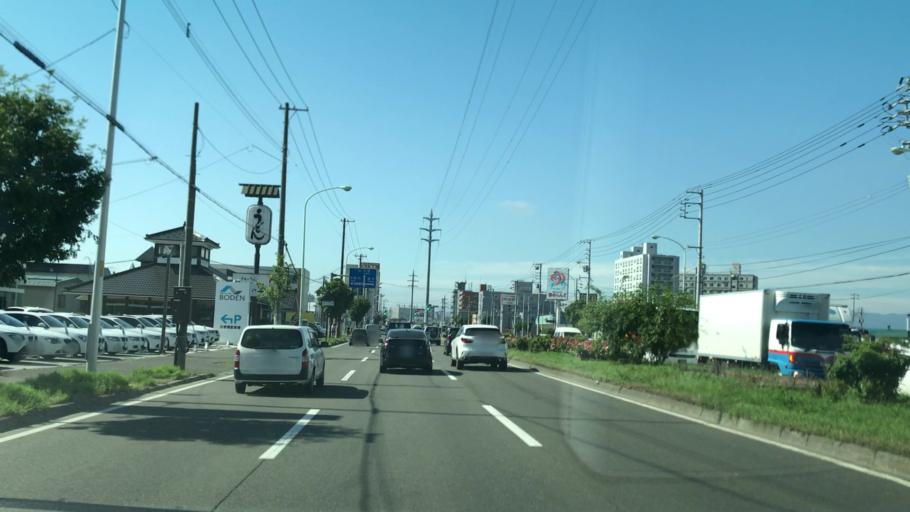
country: JP
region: Hokkaido
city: Sapporo
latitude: 43.0693
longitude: 141.4088
